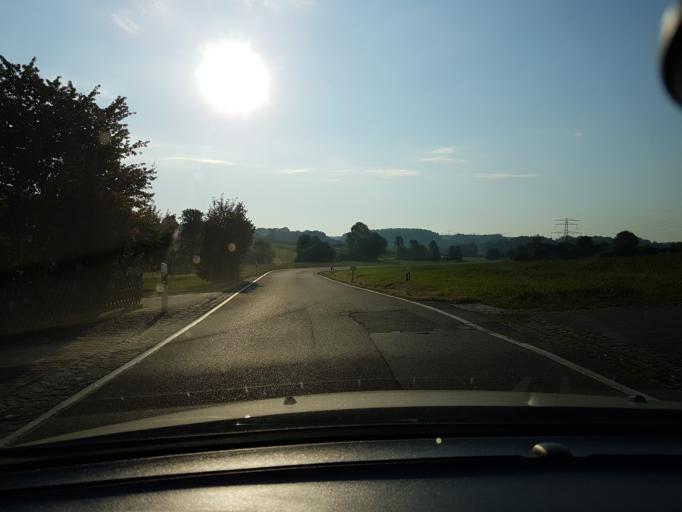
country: DE
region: Bavaria
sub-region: Upper Bavaria
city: Egglkofen
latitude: 48.4163
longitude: 12.4854
